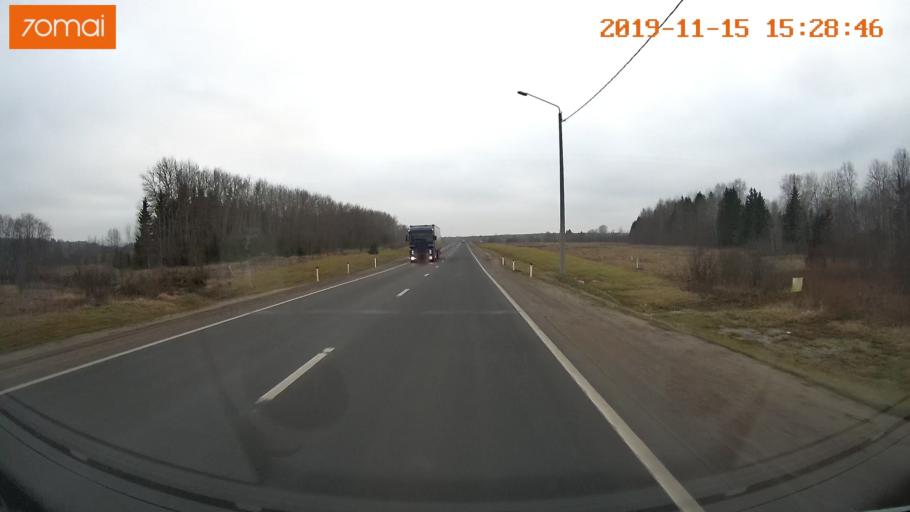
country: RU
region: Jaroslavl
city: Danilov
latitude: 58.1285
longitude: 40.1302
